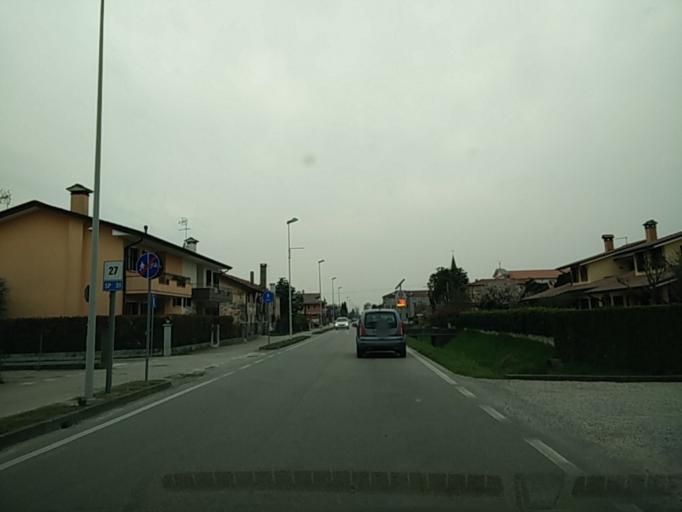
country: IT
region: Veneto
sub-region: Provincia di Padova
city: Massanzago-Ca' Baglioni-San Dono
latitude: 45.5542
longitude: 12.0318
